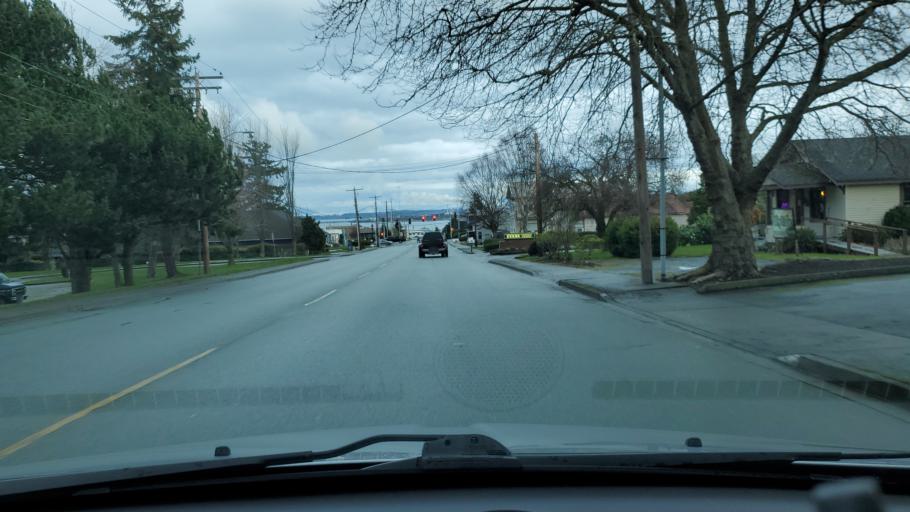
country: US
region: Washington
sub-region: Skagit County
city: Anacortes
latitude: 48.4964
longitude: -122.6153
